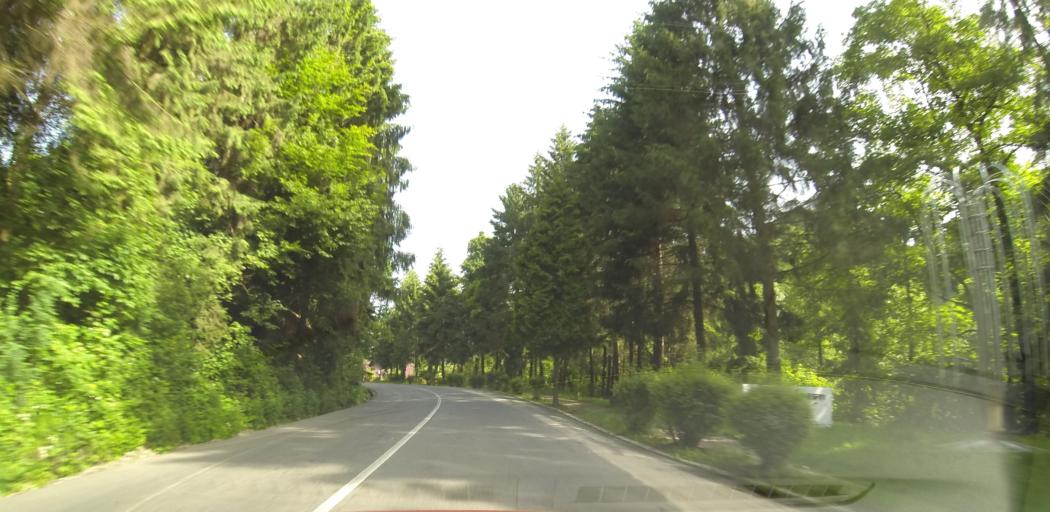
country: RO
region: Valcea
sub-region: Oras Baile Olanesti
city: Livadia
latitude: 45.1982
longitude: 24.2507
